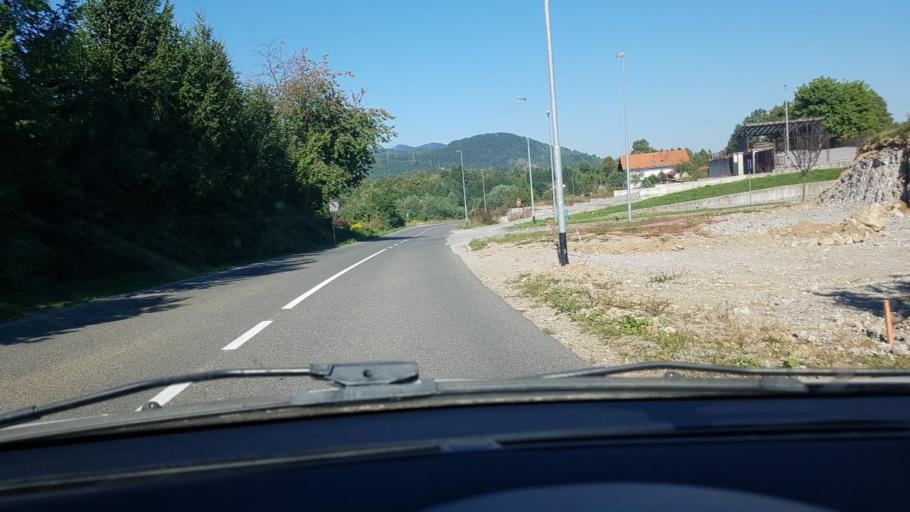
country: HR
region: Primorsko-Goranska
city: Vrbovsko
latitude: 45.3685
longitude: 15.0806
